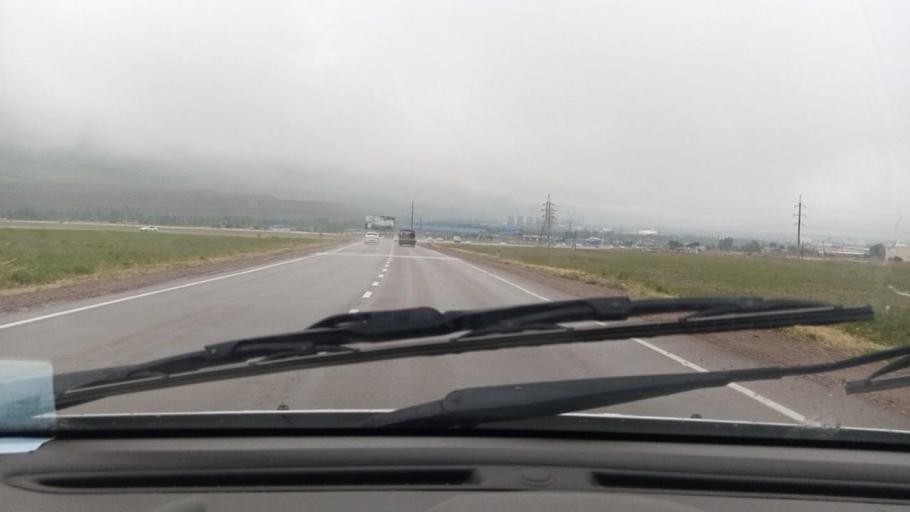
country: UZ
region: Toshkent
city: Angren
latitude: 41.0375
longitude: 70.1440
